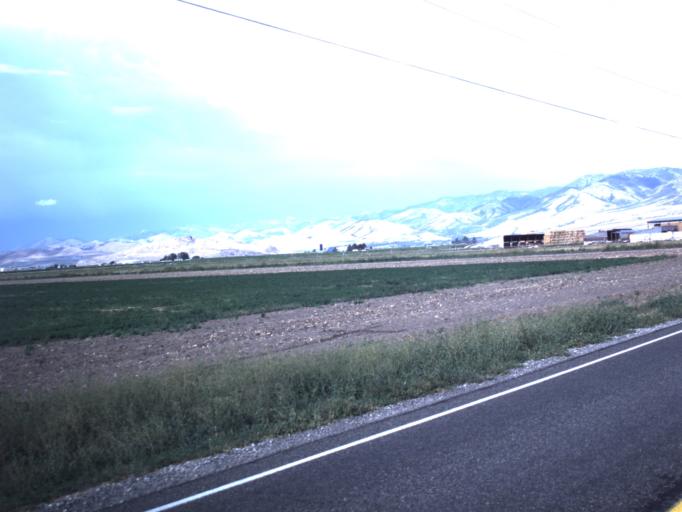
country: US
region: Utah
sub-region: Cache County
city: Lewiston
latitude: 41.9756
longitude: -111.8894
